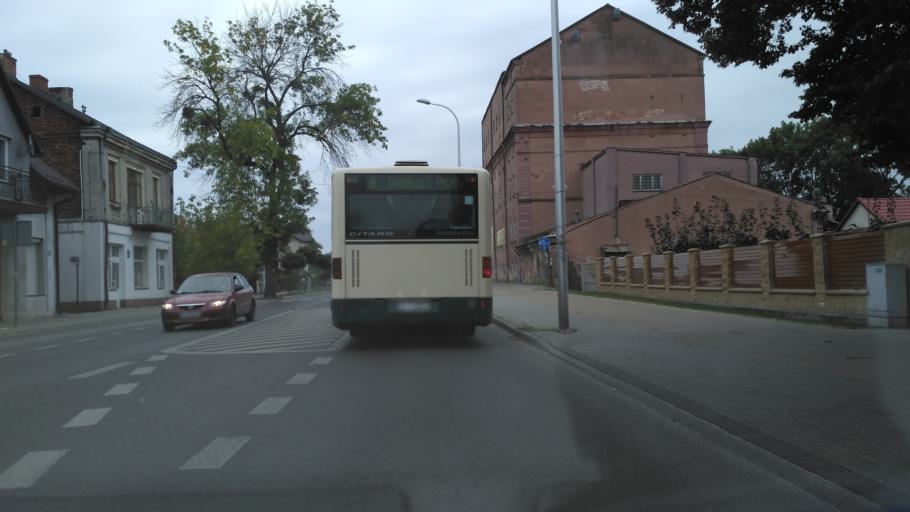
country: PL
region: Lublin Voivodeship
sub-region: Chelm
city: Chelm
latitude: 51.1382
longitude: 23.4605
